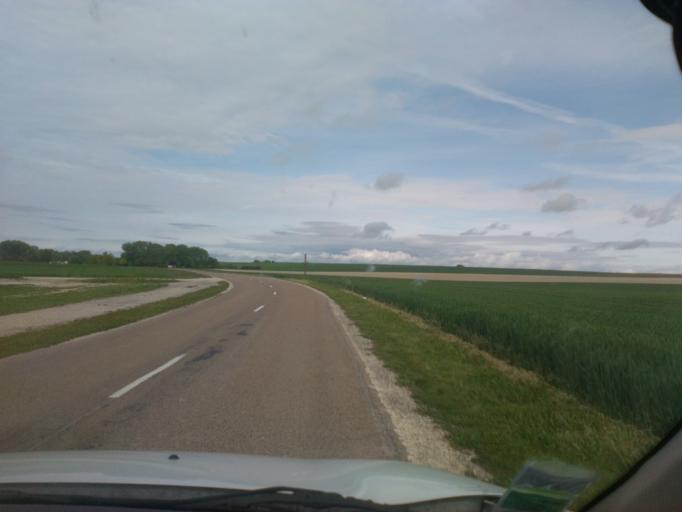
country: FR
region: Champagne-Ardenne
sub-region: Departement de l'Aube
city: Marigny-le-Chatel
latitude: 48.3627
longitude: 3.7213
